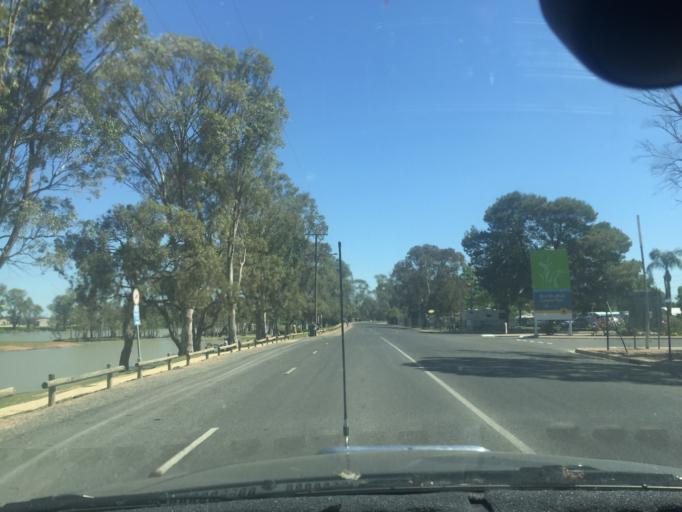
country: AU
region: South Australia
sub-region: Berri and Barmera
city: Berri
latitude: -34.2866
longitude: 140.6105
